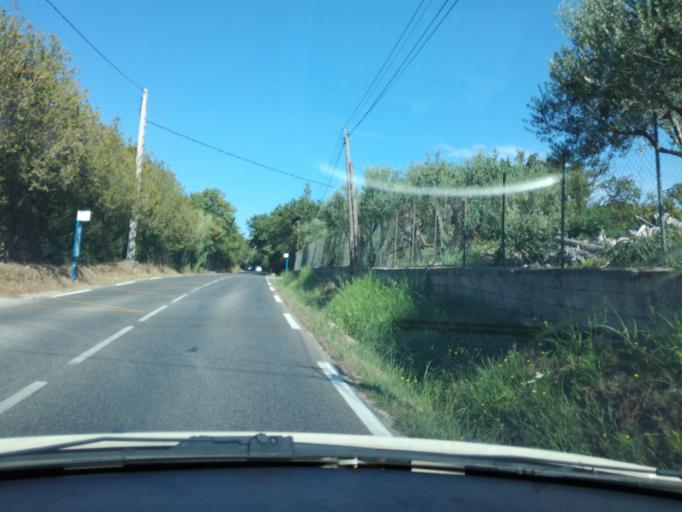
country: FR
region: Provence-Alpes-Cote d'Azur
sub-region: Departement du Var
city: La Crau
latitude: 43.1318
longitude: 6.0855
